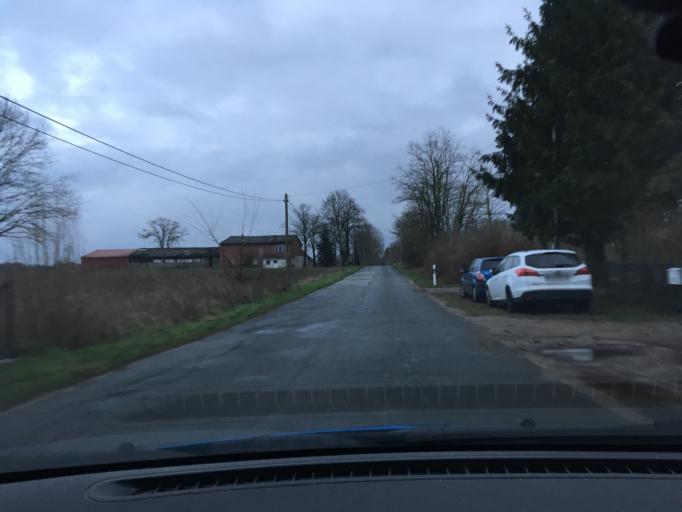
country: DE
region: Mecklenburg-Vorpommern
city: Nostorf
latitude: 53.3927
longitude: 10.6863
